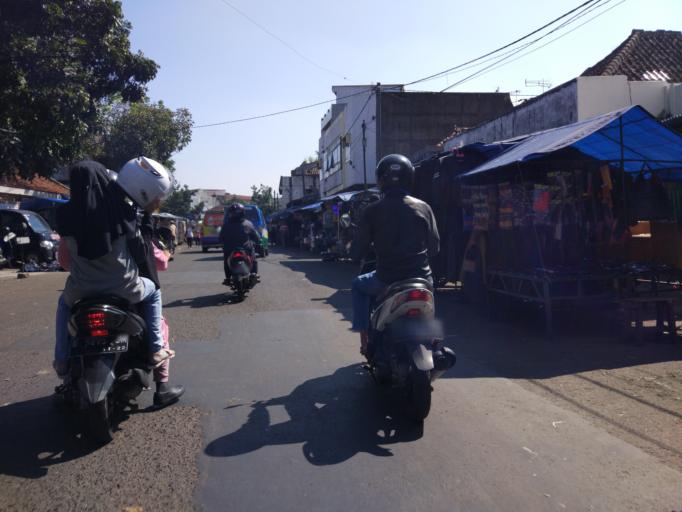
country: ID
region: West Java
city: Bandung
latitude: -6.9323
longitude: 107.6021
